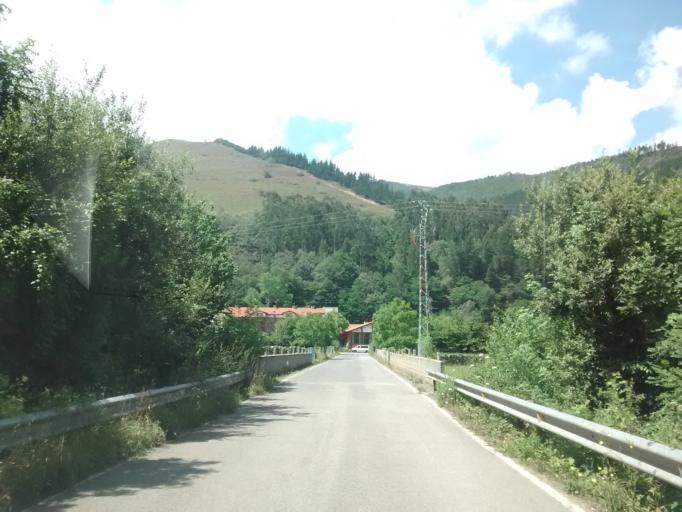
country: ES
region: Cantabria
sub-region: Provincia de Cantabria
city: Ruente
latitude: 43.2004
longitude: -4.3030
